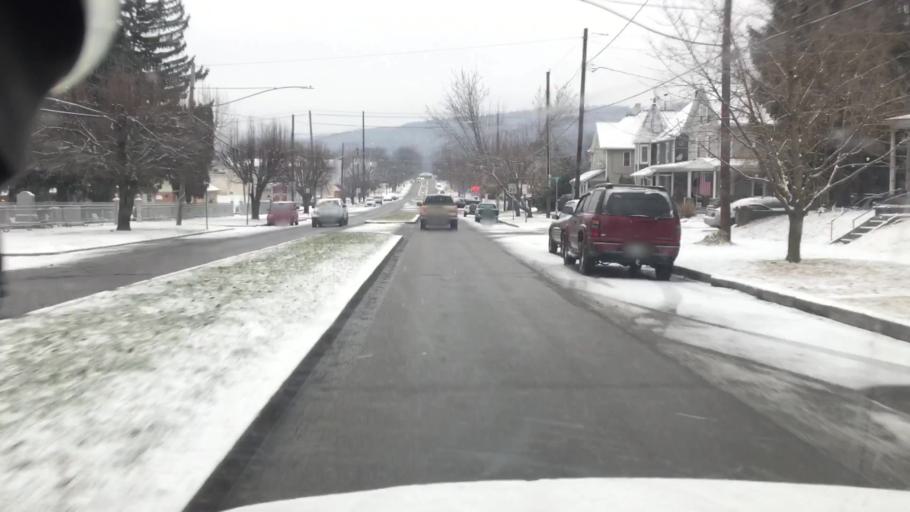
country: US
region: Pennsylvania
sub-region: Columbia County
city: Berwick
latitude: 41.0590
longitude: -76.2371
